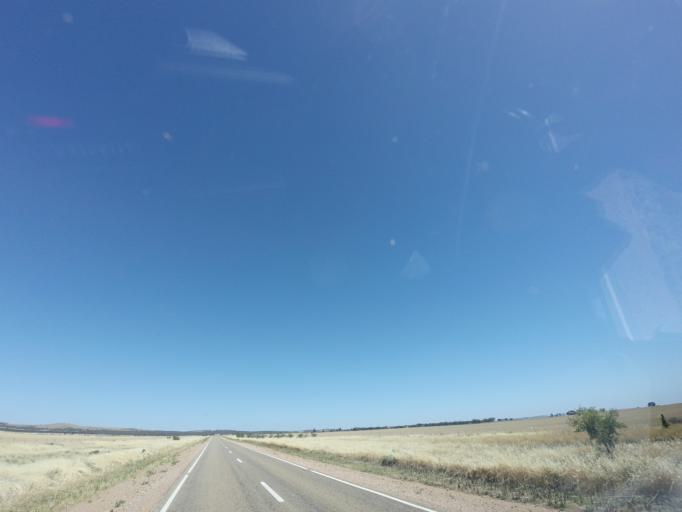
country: AU
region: South Australia
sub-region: Peterborough
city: Peterborough
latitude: -32.8472
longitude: 138.7298
